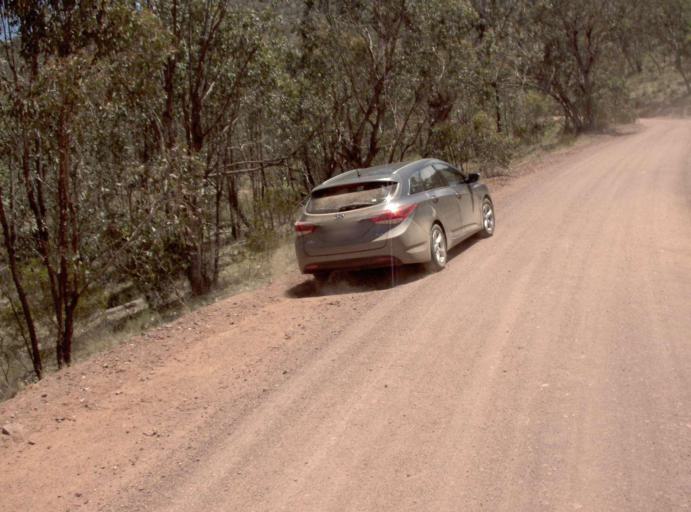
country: AU
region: New South Wales
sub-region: Snowy River
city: Jindabyne
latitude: -36.9193
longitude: 148.3987
